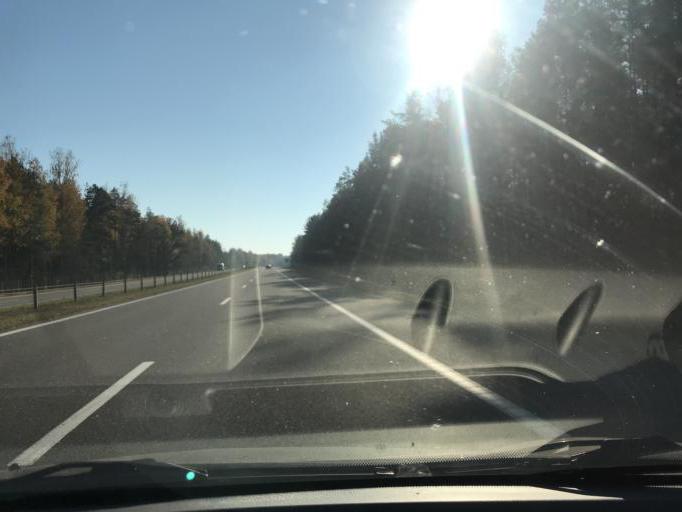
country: BY
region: Minsk
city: Pukhavichy
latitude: 53.4965
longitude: 28.3442
